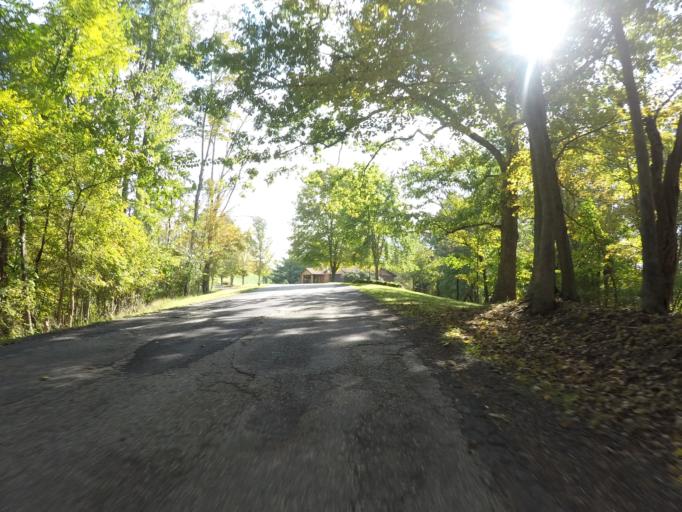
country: US
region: West Virginia
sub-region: Wayne County
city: Lavalette
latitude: 38.3630
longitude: -82.4640
